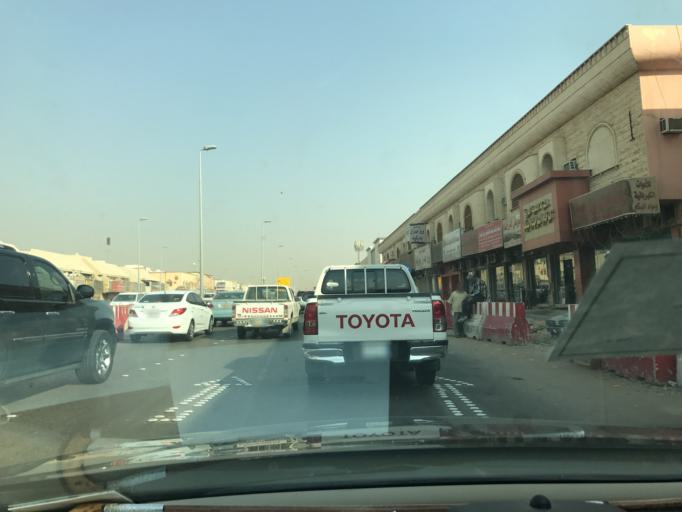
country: SA
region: Ar Riyad
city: Riyadh
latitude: 24.7549
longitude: 46.7688
